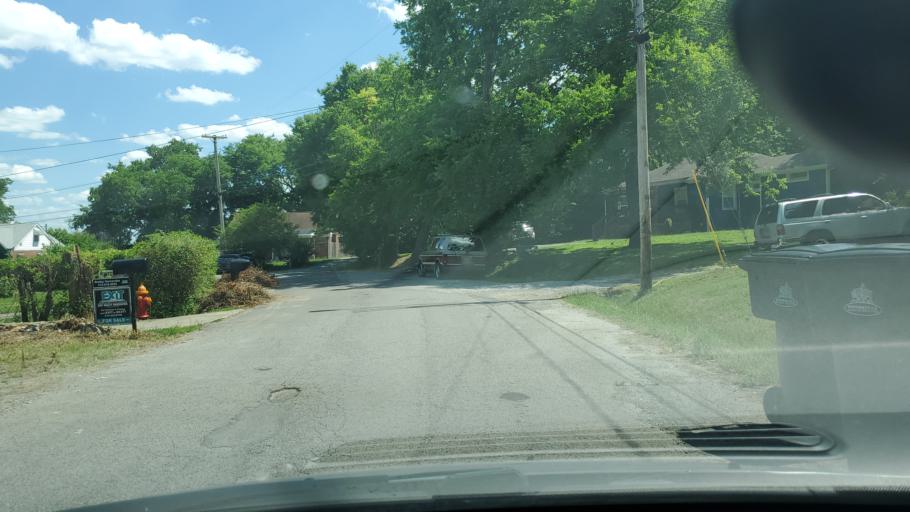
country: US
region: Tennessee
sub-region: Davidson County
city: Nashville
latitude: 36.2021
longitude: -86.7605
